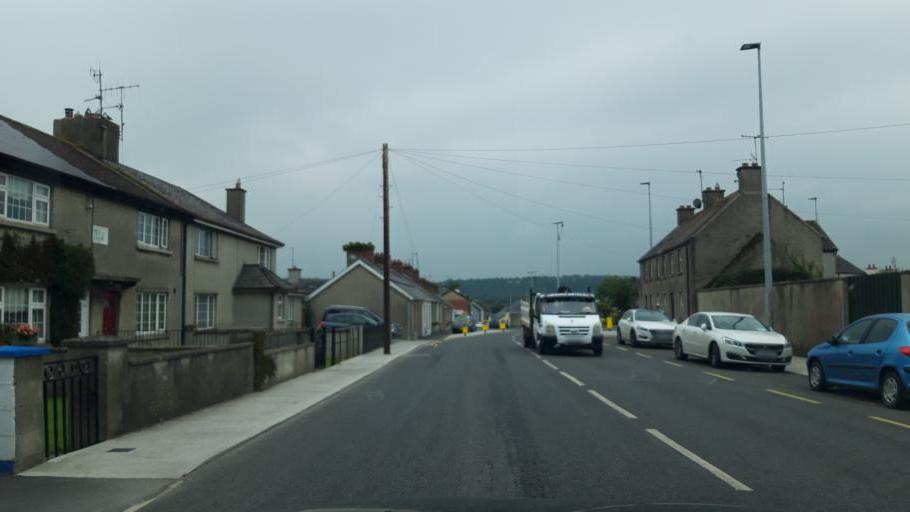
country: IE
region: Munster
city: Fethard
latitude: 52.4685
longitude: -7.6914
